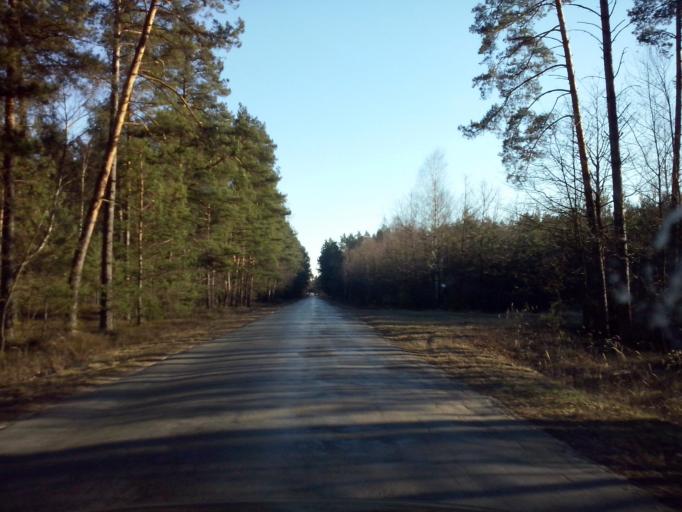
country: PL
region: Subcarpathian Voivodeship
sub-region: Powiat nizanski
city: Harasiuki
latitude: 50.4887
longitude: 22.4749
